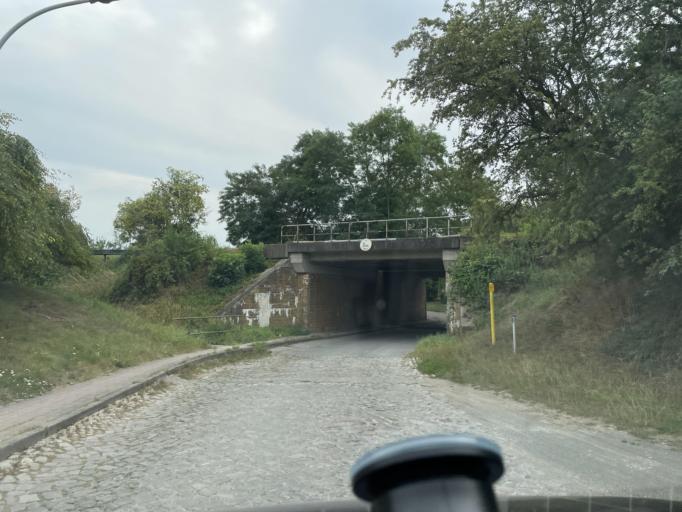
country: DE
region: Saxony-Anhalt
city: Calbe
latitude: 51.9067
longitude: 11.7602
